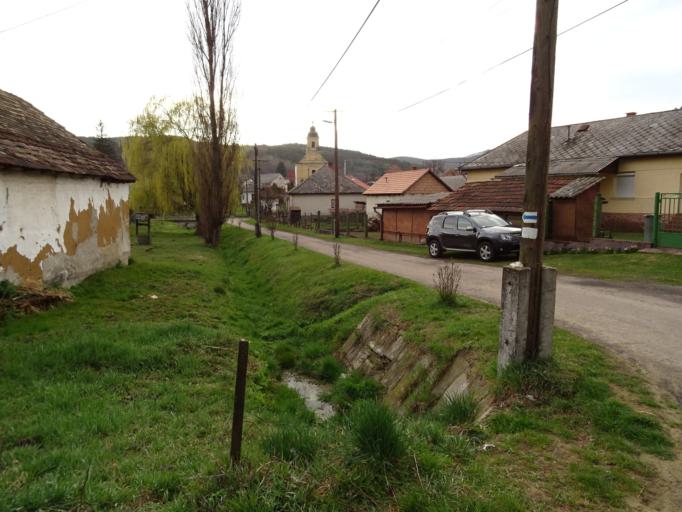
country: HU
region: Nograd
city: Matraterenye
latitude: 48.1000
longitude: 19.9364
